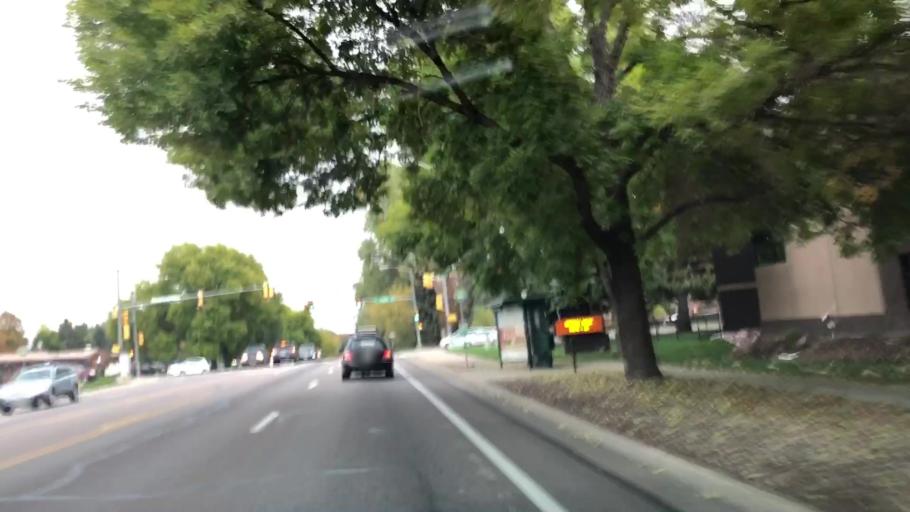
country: US
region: Colorado
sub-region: Larimer County
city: Fort Collins
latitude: 40.5628
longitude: -105.0579
